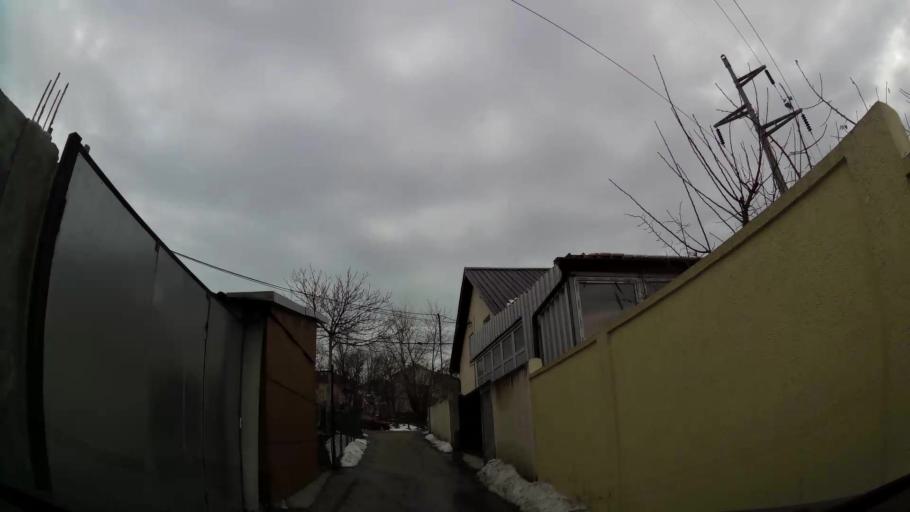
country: RS
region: Central Serbia
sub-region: Belgrade
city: Rakovica
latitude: 44.7440
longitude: 20.3997
